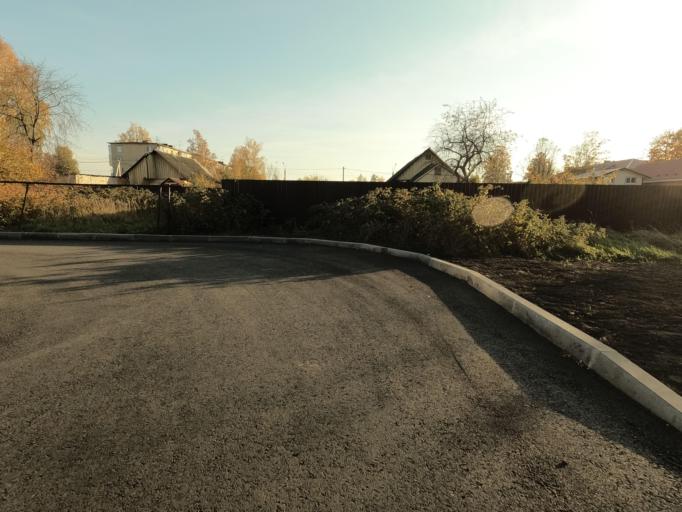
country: RU
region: Leningrad
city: Mga
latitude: 59.7597
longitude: 31.0678
